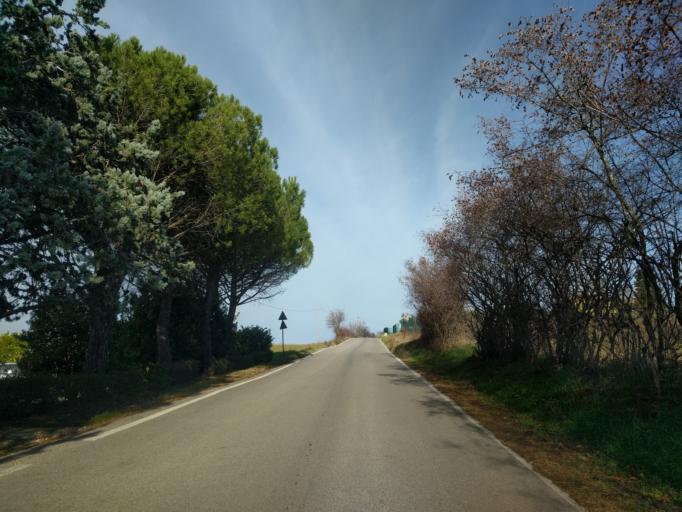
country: IT
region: The Marches
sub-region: Provincia di Pesaro e Urbino
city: Cuccurano
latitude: 43.7979
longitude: 12.9508
